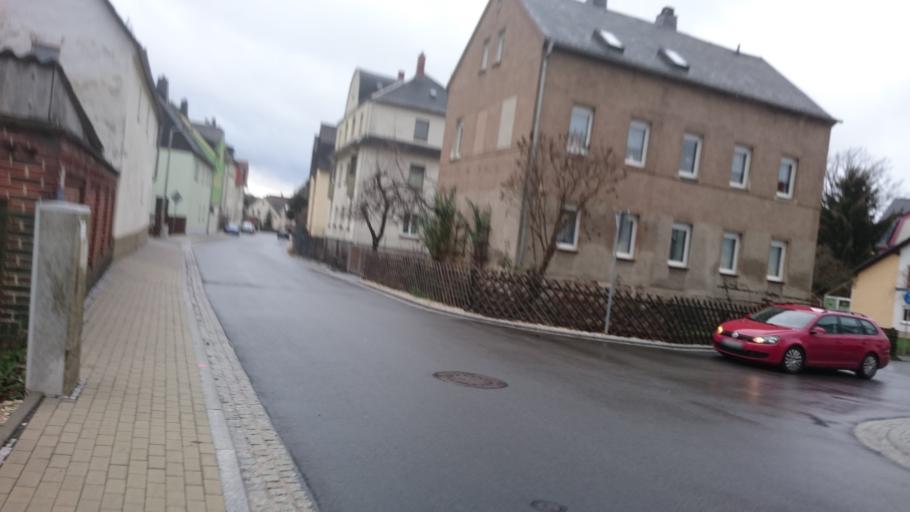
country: DE
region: Saxony
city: Zwickau
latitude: 50.7578
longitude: 12.4949
